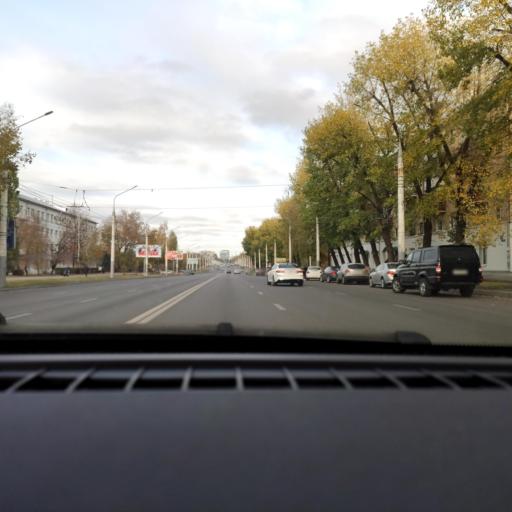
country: RU
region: Voronezj
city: Voronezh
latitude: 51.6563
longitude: 39.2444
